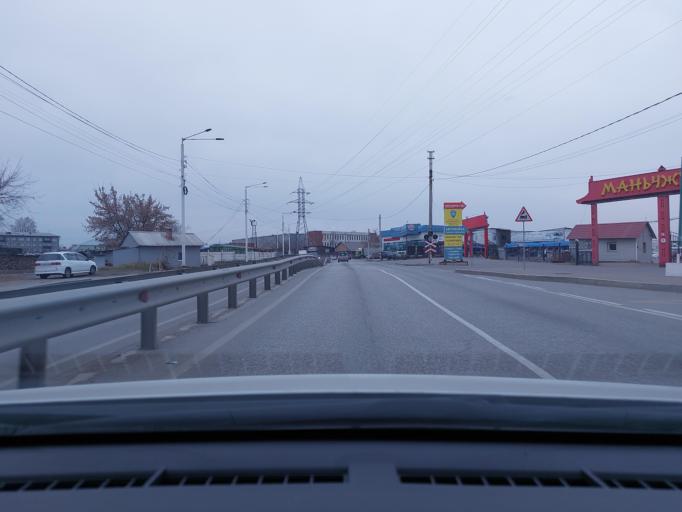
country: RU
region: Irkutsk
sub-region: Irkutskiy Rayon
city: Irkutsk
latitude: 52.3373
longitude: 104.2329
